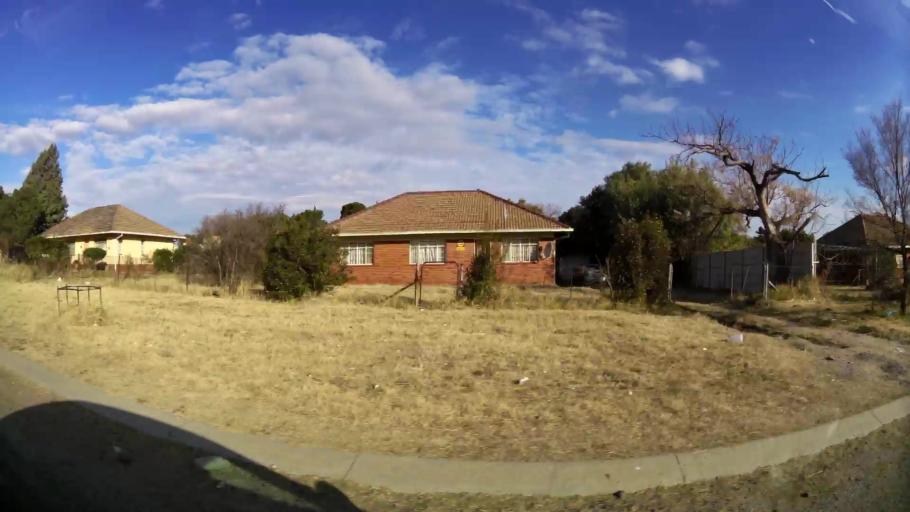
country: ZA
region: Orange Free State
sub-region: Lejweleputswa District Municipality
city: Welkom
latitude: -27.9873
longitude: 26.7074
